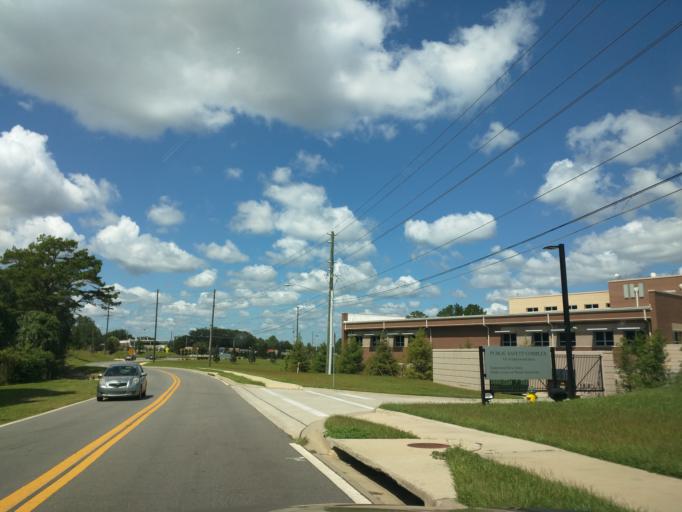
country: US
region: Florida
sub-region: Leon County
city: Tallahassee
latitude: 30.4506
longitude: -84.2224
